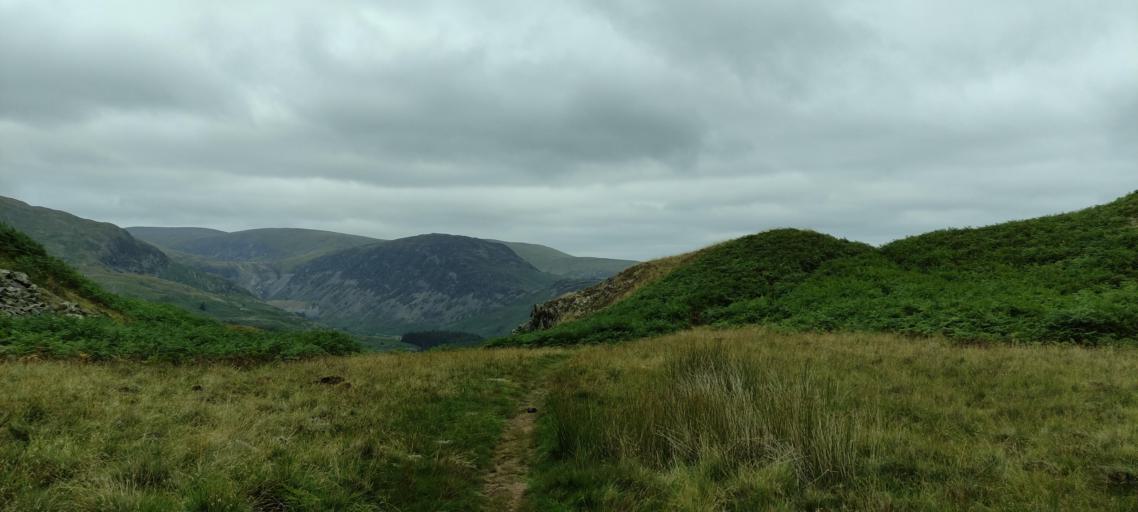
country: GB
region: England
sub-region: Cumbria
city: Ambleside
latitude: 54.5260
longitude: -2.9393
